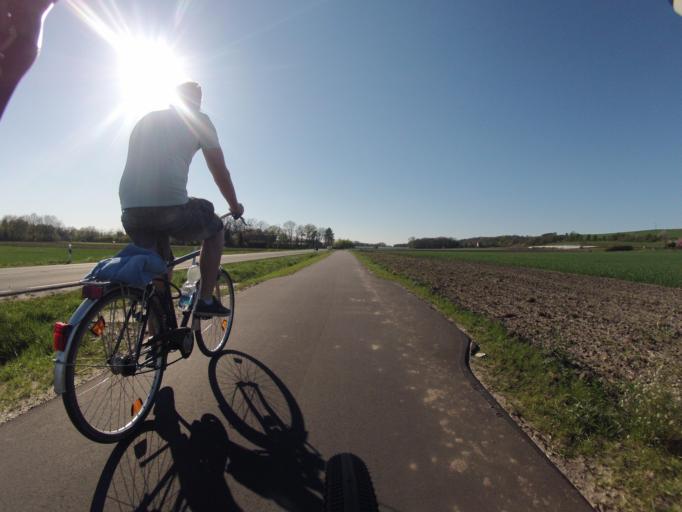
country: DE
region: North Rhine-Westphalia
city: Ibbenburen
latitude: 52.2228
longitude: 7.7341
